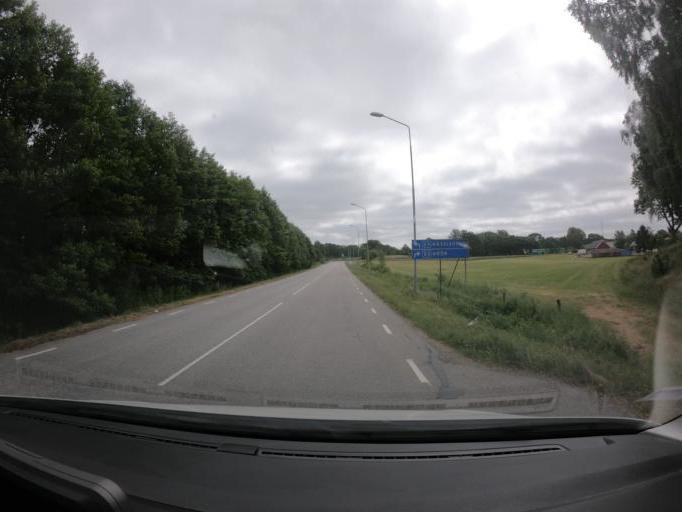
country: SE
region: Skane
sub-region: Hassleholms Kommun
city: Sosdala
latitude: 56.0071
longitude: 13.6481
